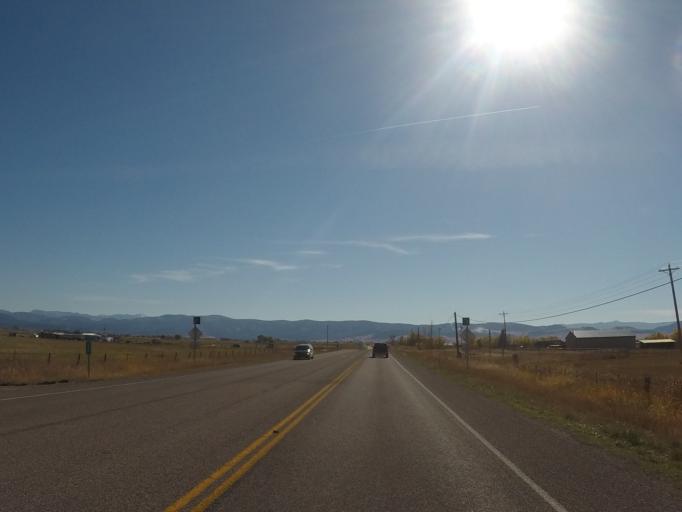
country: US
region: Montana
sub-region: Lake County
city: Ronan
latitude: 47.3836
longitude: -114.0969
